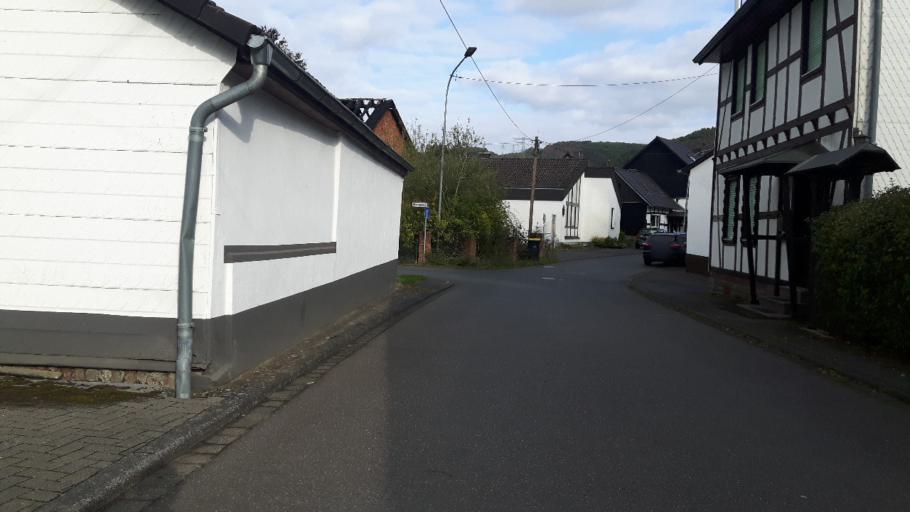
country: DE
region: Rheinland-Pfalz
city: Werkhausen
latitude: 50.7593
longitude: 7.5141
